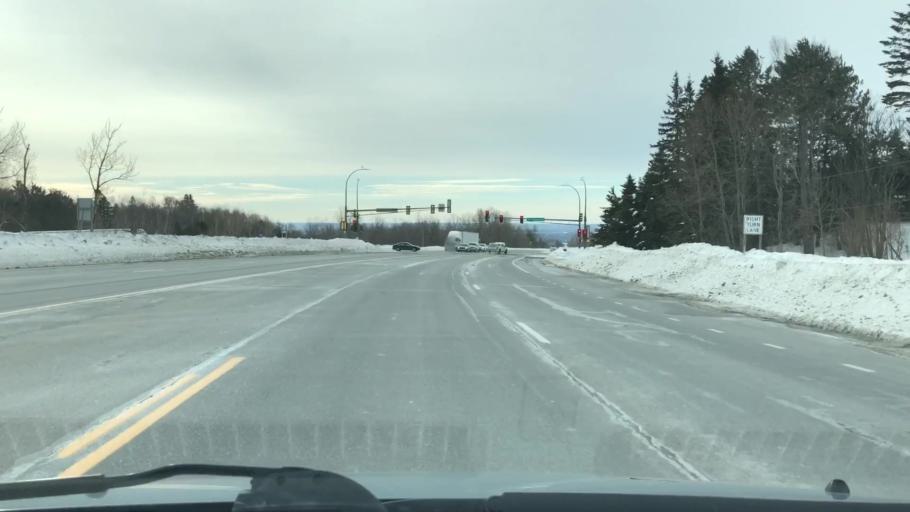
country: US
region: Minnesota
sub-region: Saint Louis County
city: Duluth
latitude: 46.7837
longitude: -92.1391
